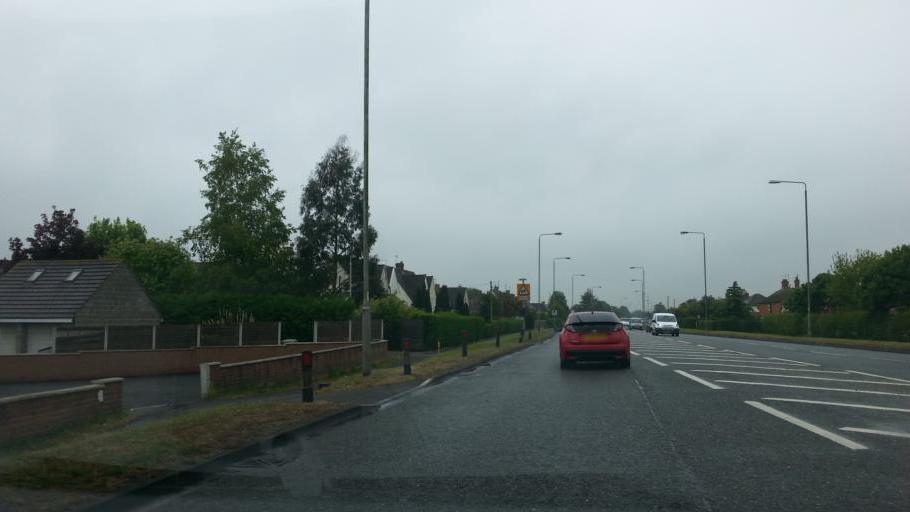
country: GB
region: England
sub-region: Nottinghamshire
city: Newark on Trent
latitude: 53.0905
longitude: -0.7911
